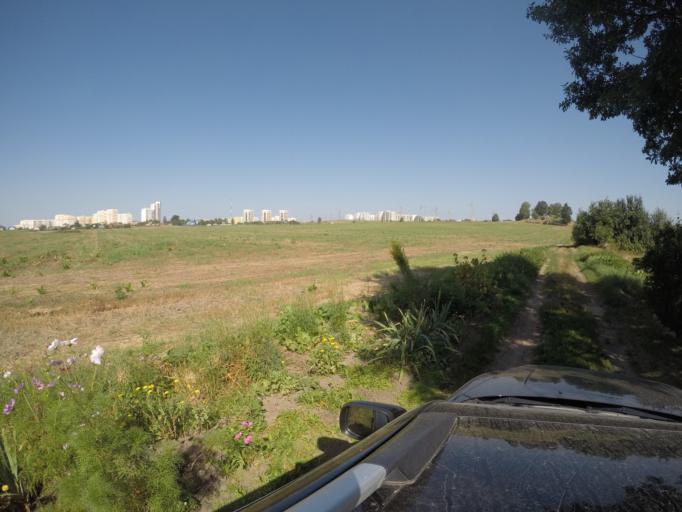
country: BY
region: Grodnenskaya
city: Hrodna
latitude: 53.7090
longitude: 23.8768
